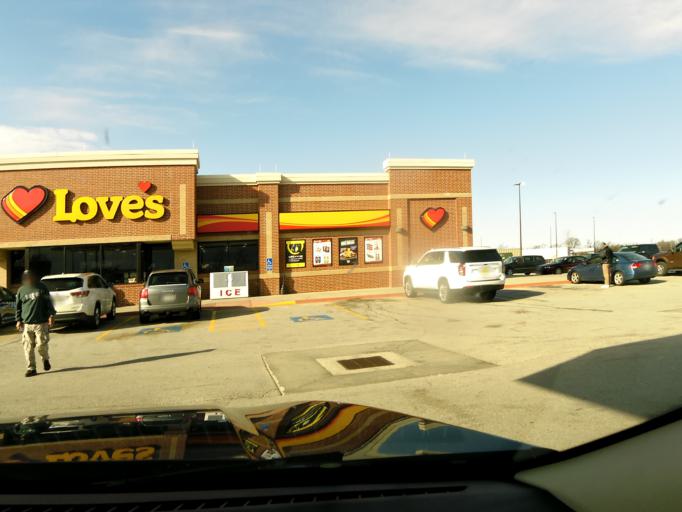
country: US
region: Missouri
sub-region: Ralls County
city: New London
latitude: 39.5740
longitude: -91.4035
